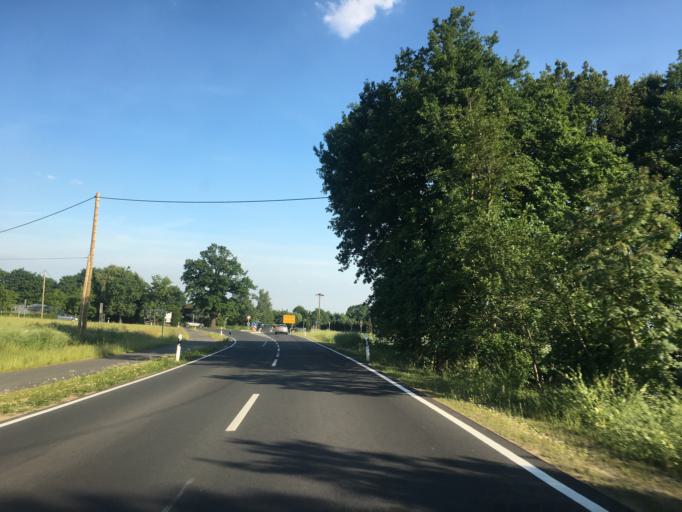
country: DE
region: North Rhine-Westphalia
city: Olfen
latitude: 51.7220
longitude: 7.4040
